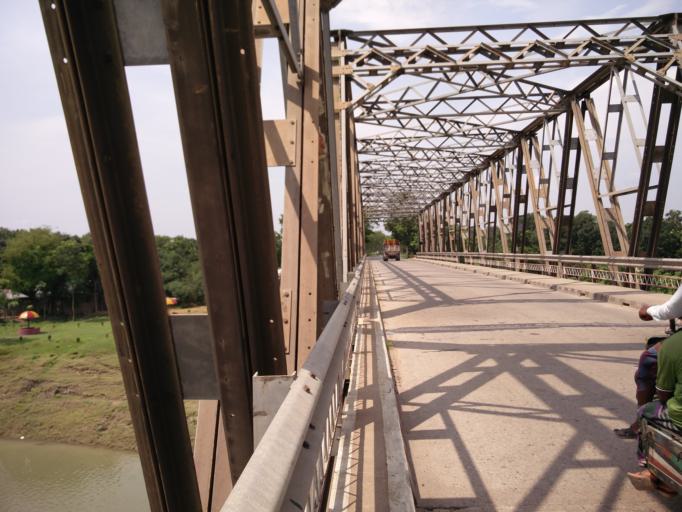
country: BD
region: Khulna
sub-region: Magura
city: Magura
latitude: 23.5401
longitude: 89.5163
